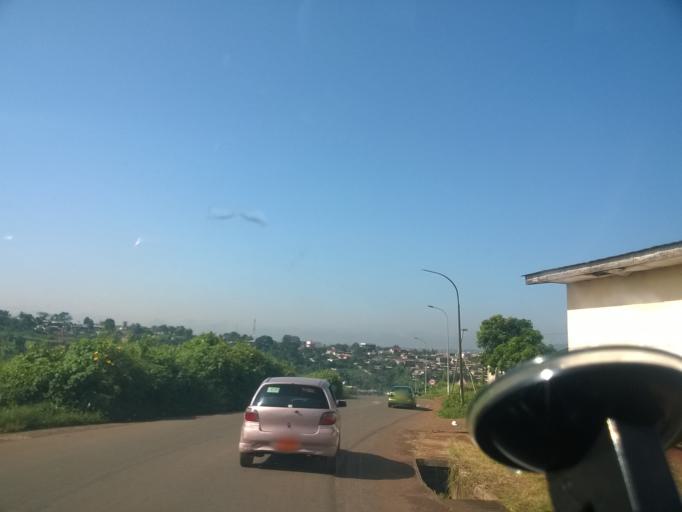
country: CM
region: Centre
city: Yaounde
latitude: 3.8511
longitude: 11.5048
